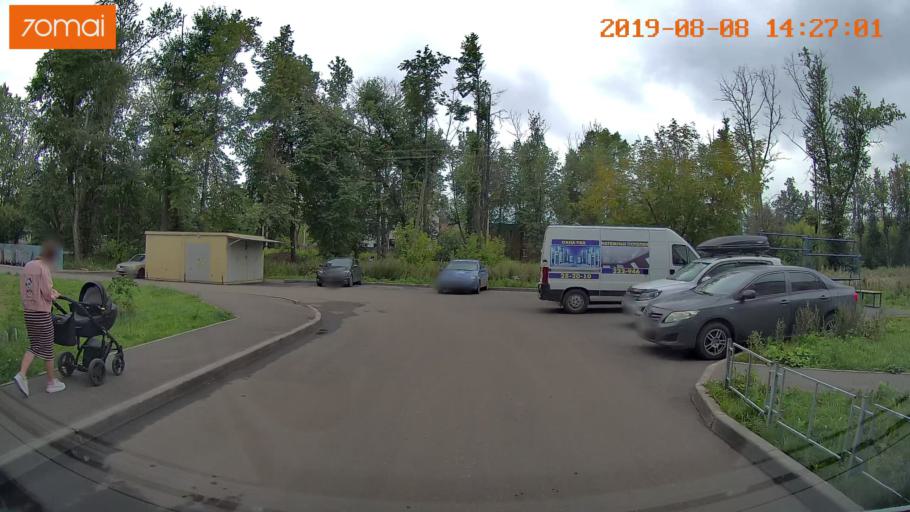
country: RU
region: Ivanovo
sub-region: Gorod Ivanovo
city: Ivanovo
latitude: 56.9987
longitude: 40.9409
